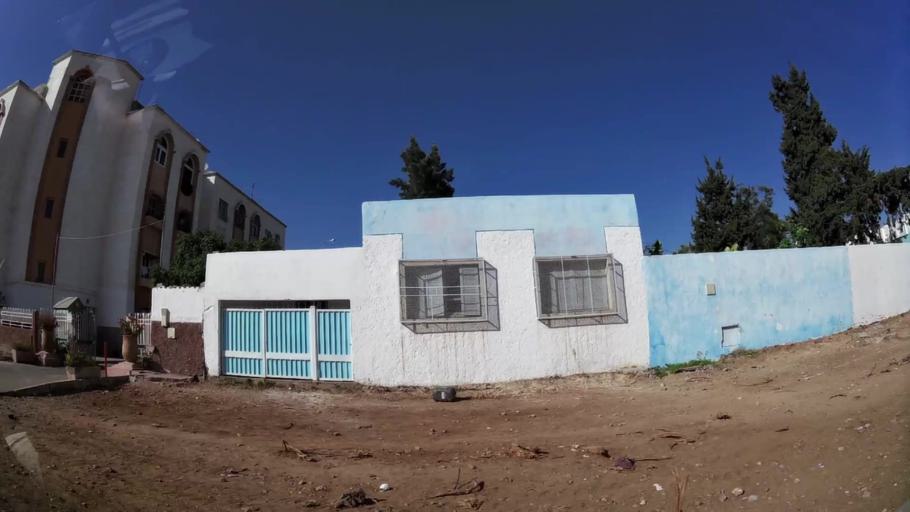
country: MA
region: Oued ed Dahab-Lagouira
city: Dakhla
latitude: 30.4176
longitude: -9.5667
